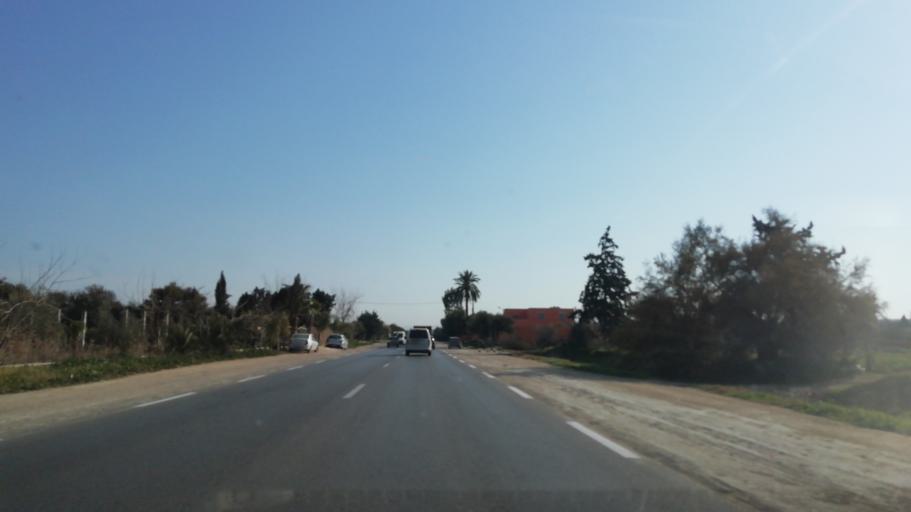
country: DZ
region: Relizane
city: Relizane
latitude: 35.7225
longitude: 0.4975
